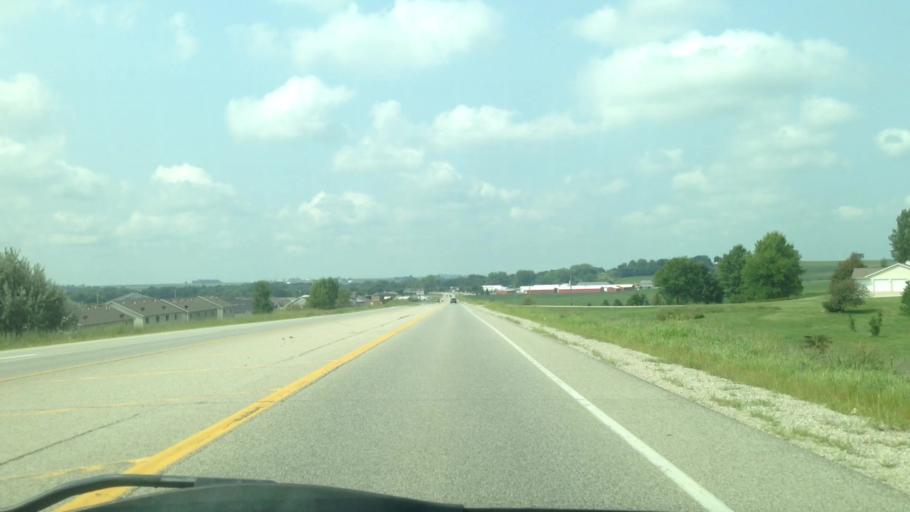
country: US
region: Iowa
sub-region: Linn County
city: Fairfax
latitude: 41.9344
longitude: -91.7664
